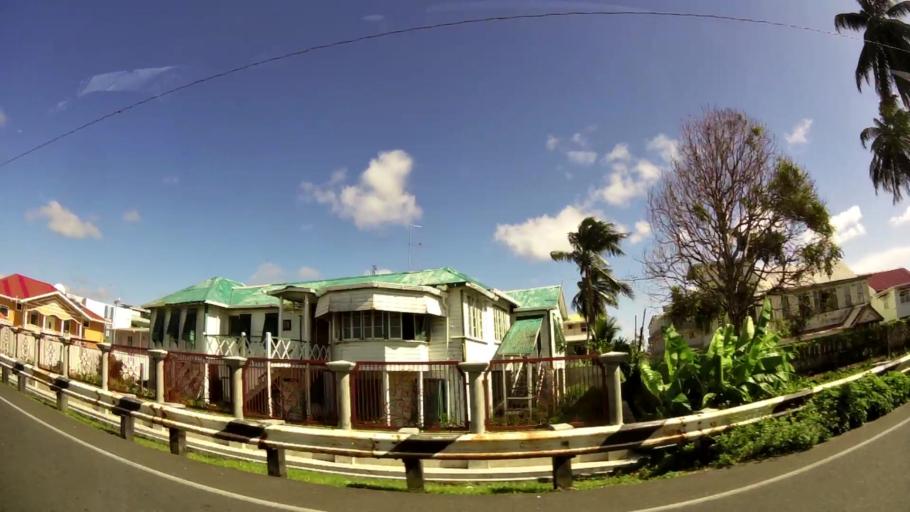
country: GY
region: Demerara-Mahaica
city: Georgetown
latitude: 6.8254
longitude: -58.1385
